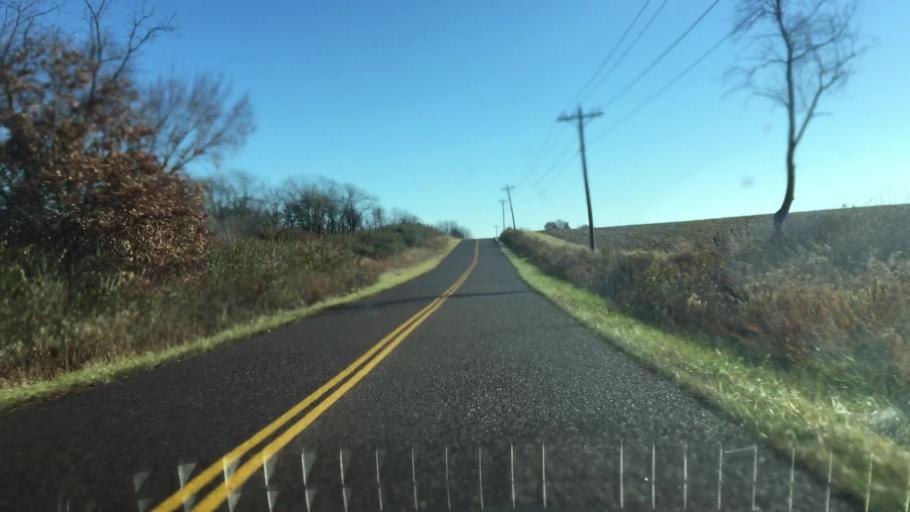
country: US
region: Missouri
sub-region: Boone County
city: Ashland
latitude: 38.8107
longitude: -92.2598
